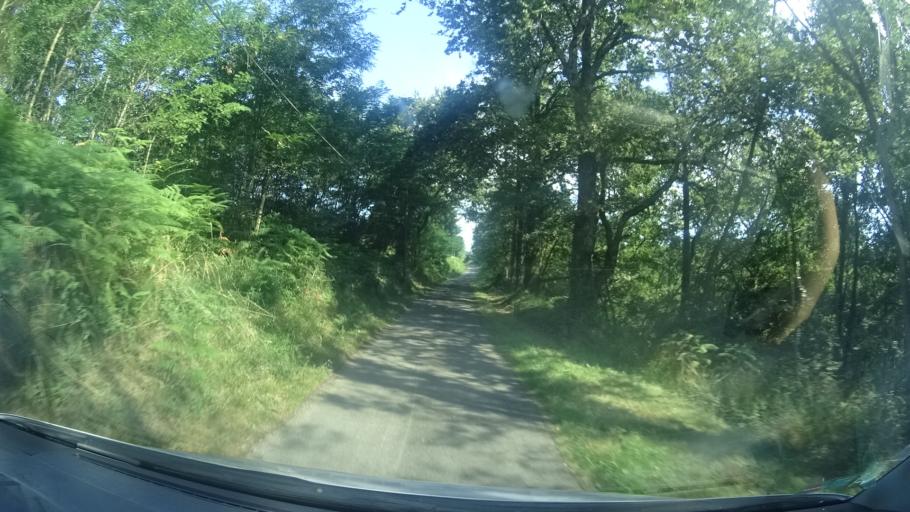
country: FR
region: Aquitaine
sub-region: Departement des Pyrenees-Atlantiques
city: Mont
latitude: 43.4965
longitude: -0.6692
